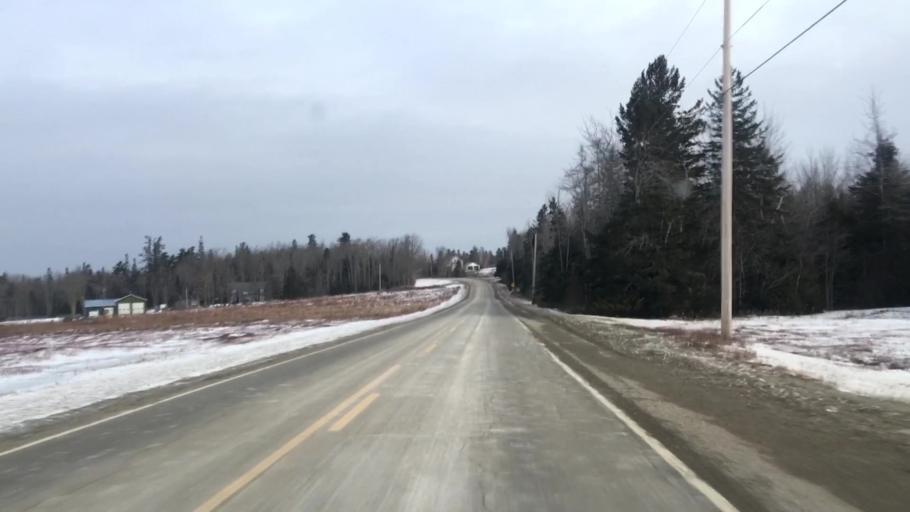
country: US
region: Maine
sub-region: Hancock County
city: Franklin
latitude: 44.7209
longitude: -68.3352
